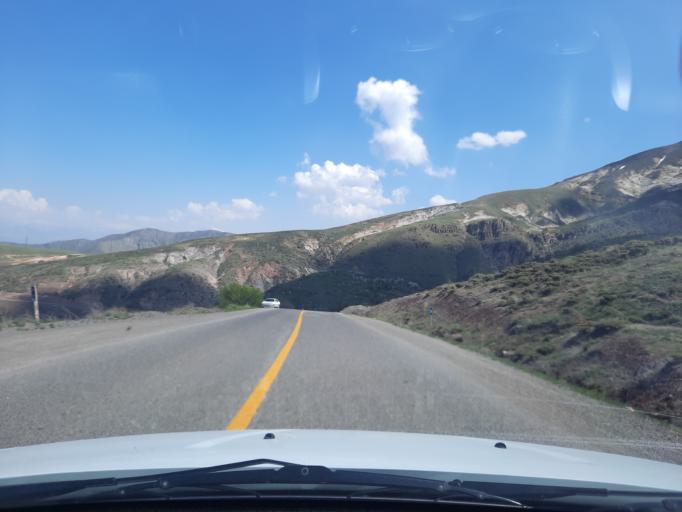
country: IR
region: Qazvin
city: Qazvin
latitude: 36.4062
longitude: 50.2221
